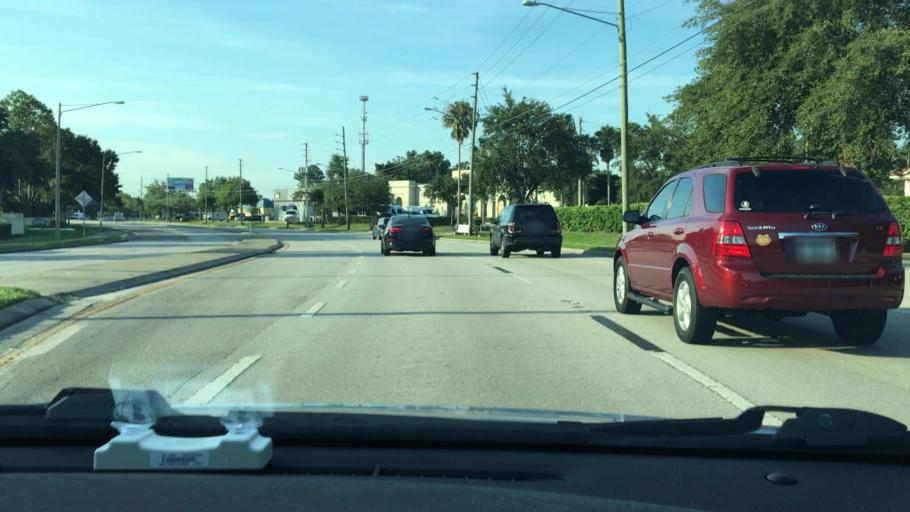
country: US
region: Florida
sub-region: Seminole County
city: Goldenrod
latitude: 28.6073
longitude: -81.2886
